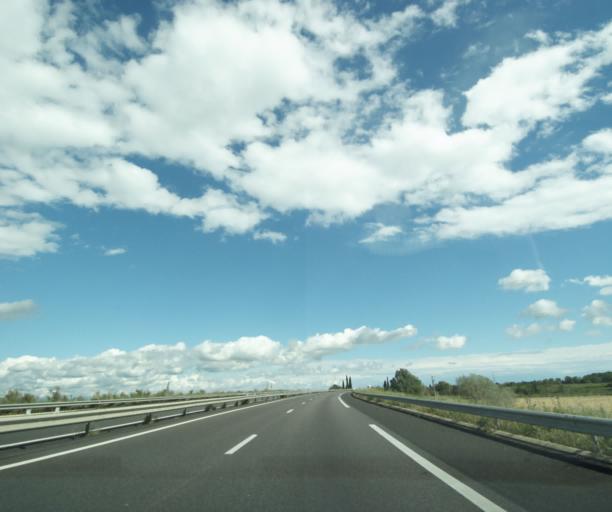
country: FR
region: Languedoc-Roussillon
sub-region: Departement du Gard
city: Bellegarde
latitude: 43.7286
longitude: 4.4987
